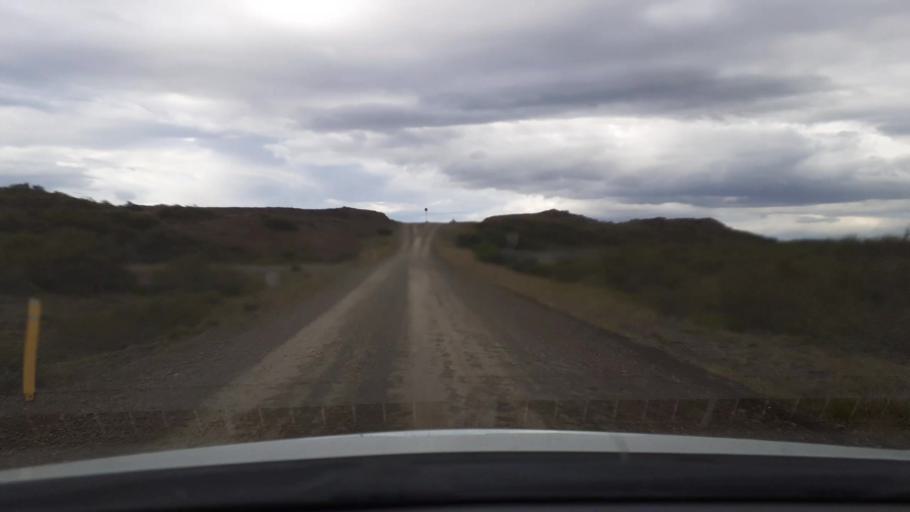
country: IS
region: West
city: Borgarnes
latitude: 64.5922
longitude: -21.9869
